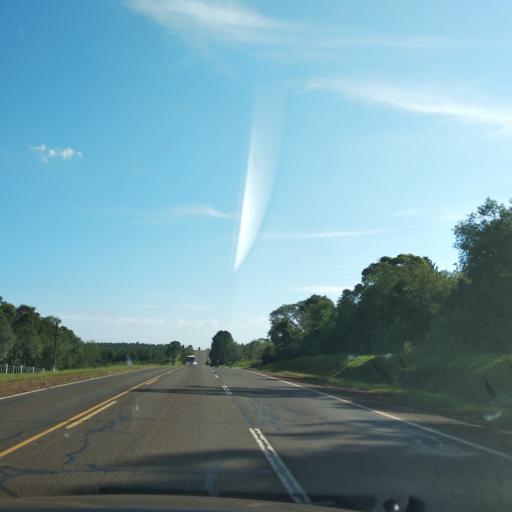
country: AR
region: Misiones
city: Santo Pipo
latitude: -27.1610
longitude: -55.4329
